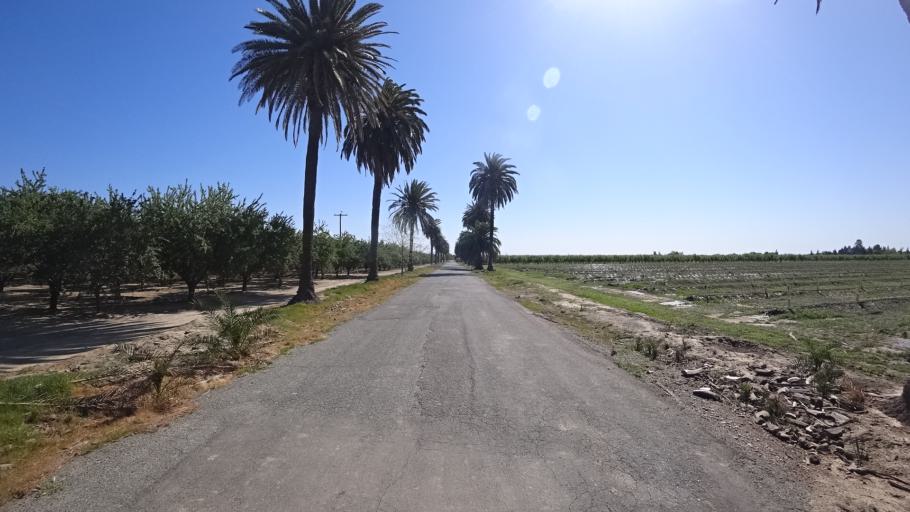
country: US
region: California
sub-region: Glenn County
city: Hamilton City
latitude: 39.7374
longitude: -122.0235
